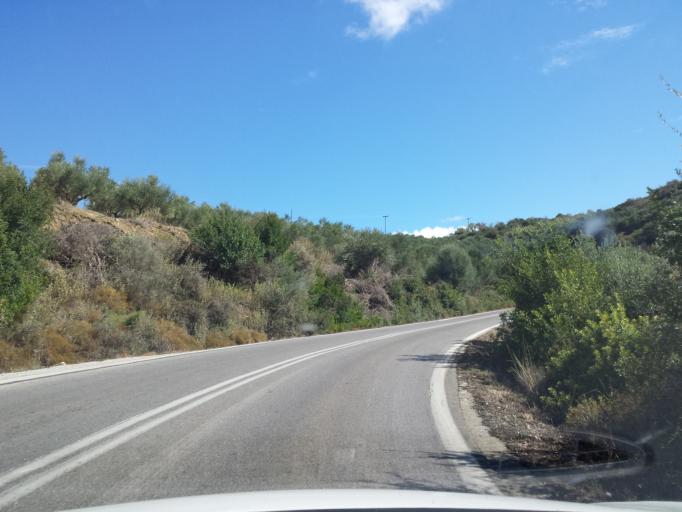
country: GR
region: Peloponnese
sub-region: Nomos Messinias
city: Pylos
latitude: 36.9409
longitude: 21.7450
